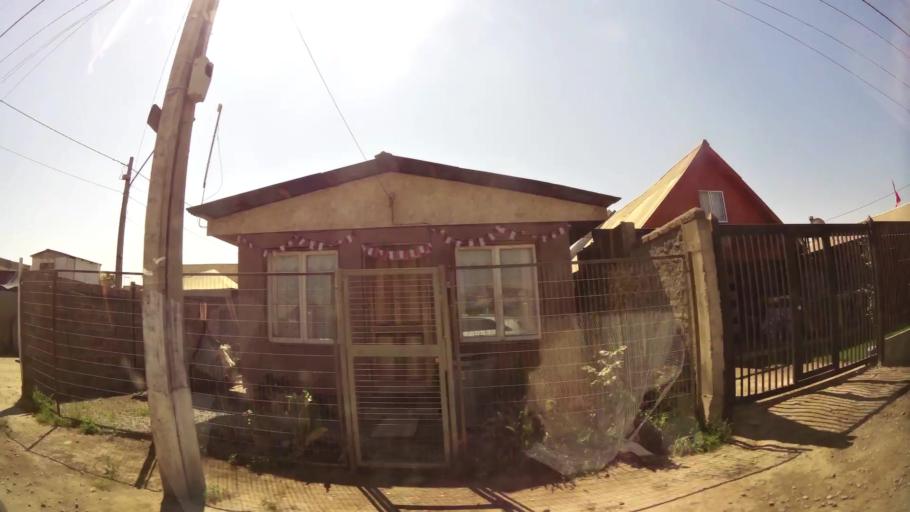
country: CL
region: Santiago Metropolitan
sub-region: Provincia de Talagante
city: Penaflor
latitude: -33.5840
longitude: -70.8075
